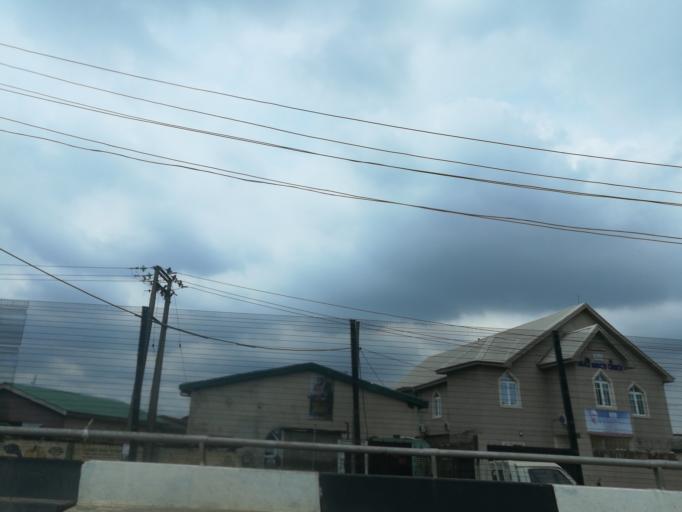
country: NG
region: Lagos
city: Somolu
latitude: 6.5437
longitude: 3.3988
